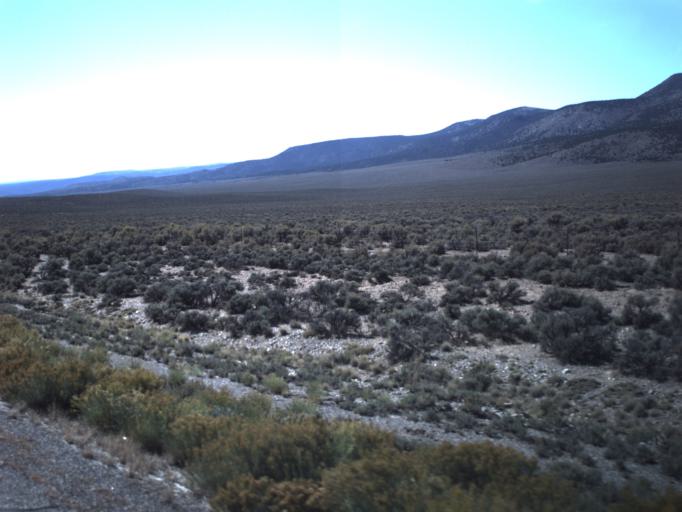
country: US
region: Utah
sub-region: Piute County
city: Junction
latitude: 38.2547
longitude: -111.9864
